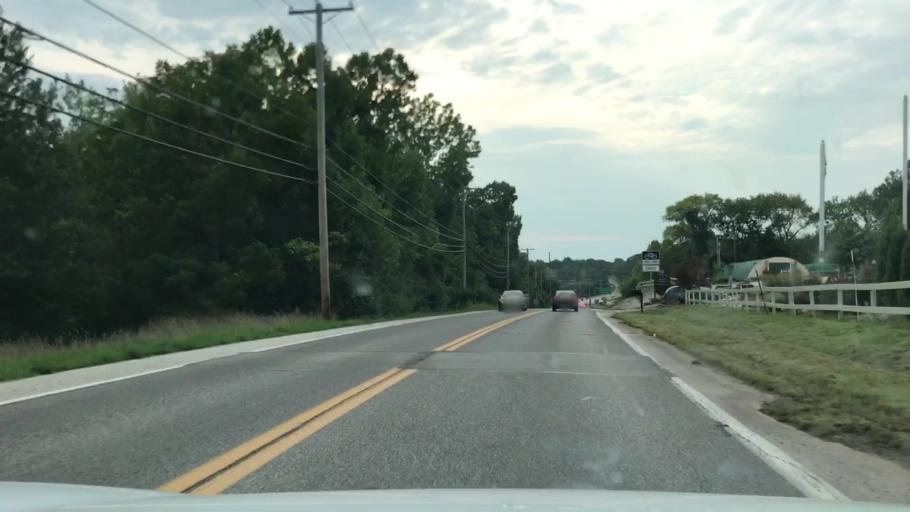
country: US
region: Missouri
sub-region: Saint Louis County
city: Chesterfield
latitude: 38.6567
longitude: -90.6151
